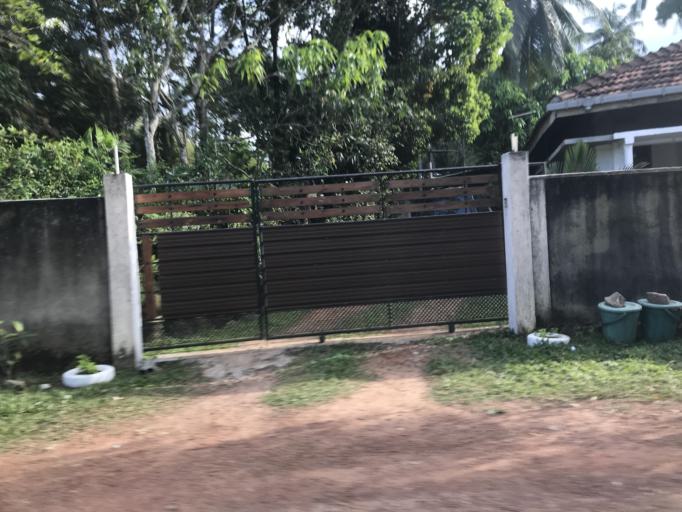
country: LK
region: Western
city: Gampaha
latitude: 7.0734
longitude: 79.9993
